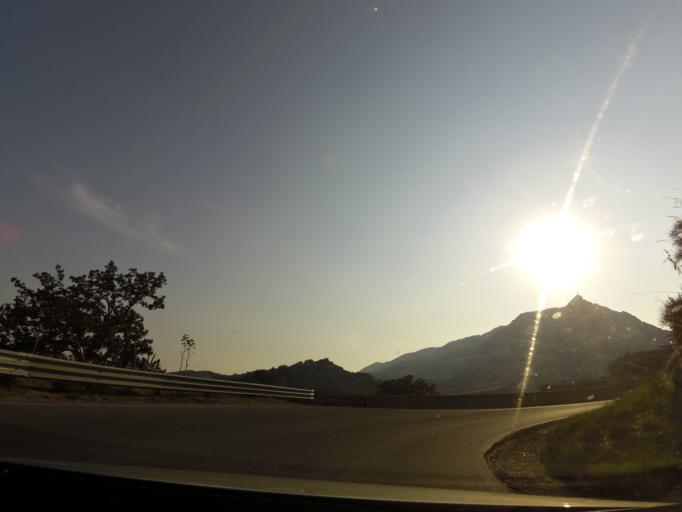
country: IT
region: Calabria
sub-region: Provincia di Reggio Calabria
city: Stilo
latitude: 38.4708
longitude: 16.4705
